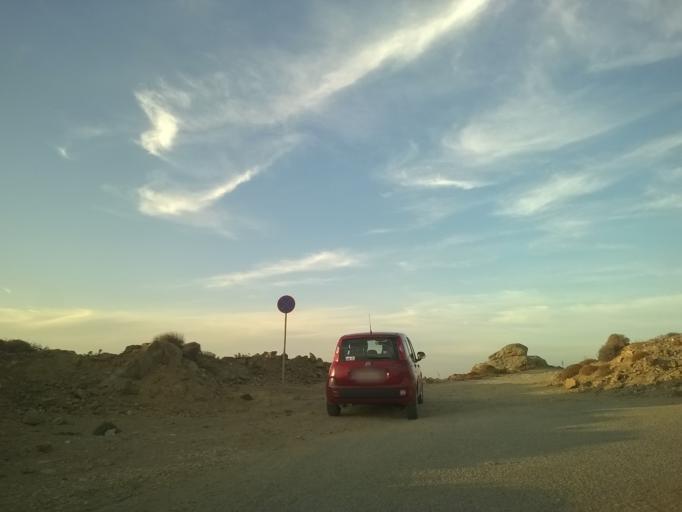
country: GR
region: South Aegean
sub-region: Nomos Kykladon
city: Naxos
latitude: 37.1109
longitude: 25.3900
